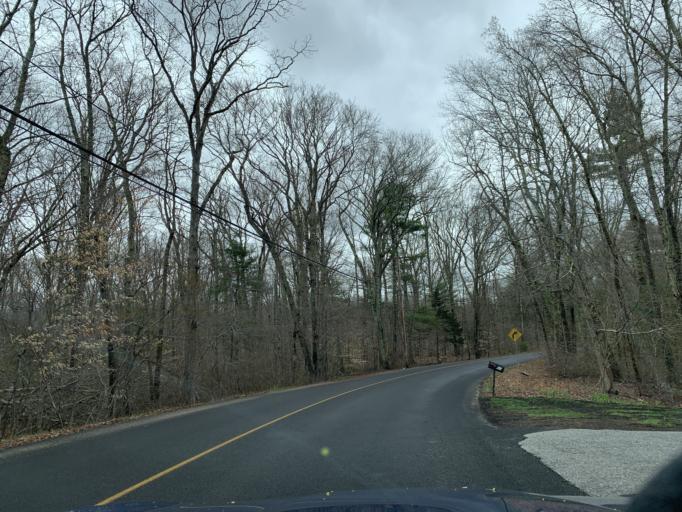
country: US
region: Massachusetts
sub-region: Bristol County
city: Rehoboth
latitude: 41.8943
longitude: -71.2119
